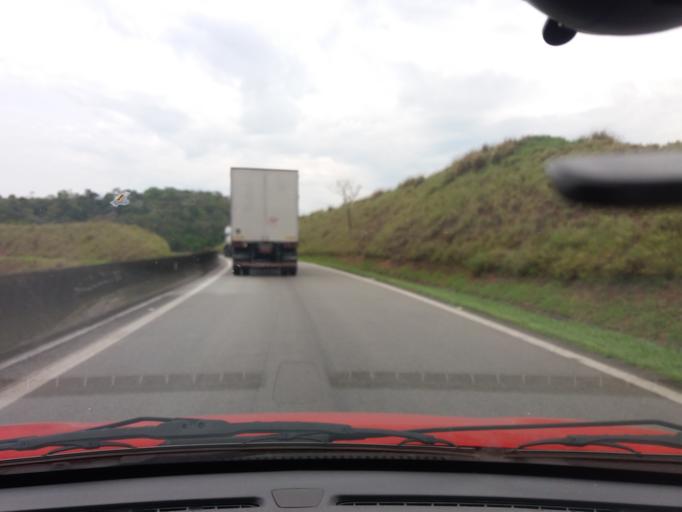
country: BR
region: Sao Paulo
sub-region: Caieiras
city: Caieiras
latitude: -23.4363
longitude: -46.7613
